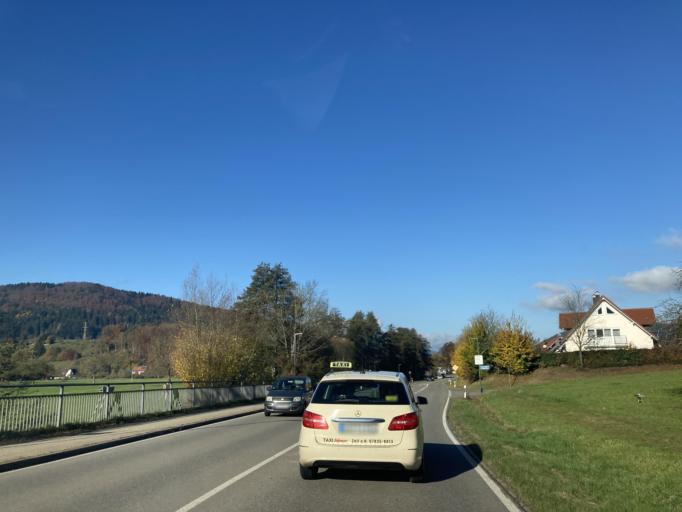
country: DE
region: Baden-Wuerttemberg
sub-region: Freiburg Region
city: Muhlenbach
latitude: 48.2689
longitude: 8.0949
